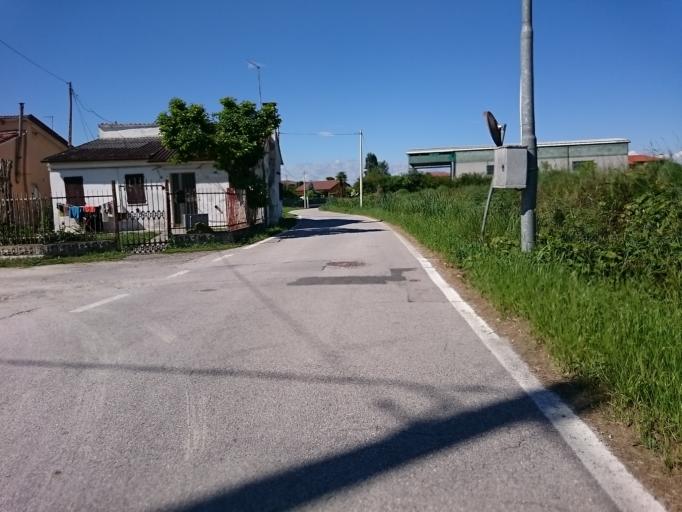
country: IT
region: Veneto
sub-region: Provincia di Padova
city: Saonara
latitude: 45.3533
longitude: 12.0034
